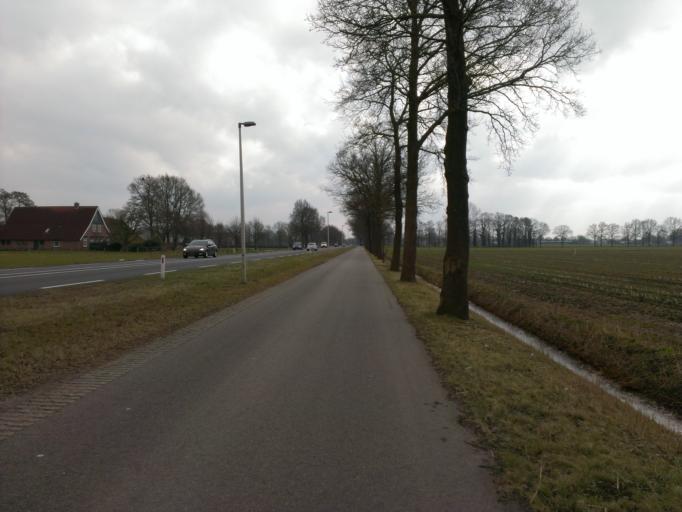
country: NL
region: Overijssel
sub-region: Gemeente Borne
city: Borne
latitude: 52.3179
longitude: 6.7314
